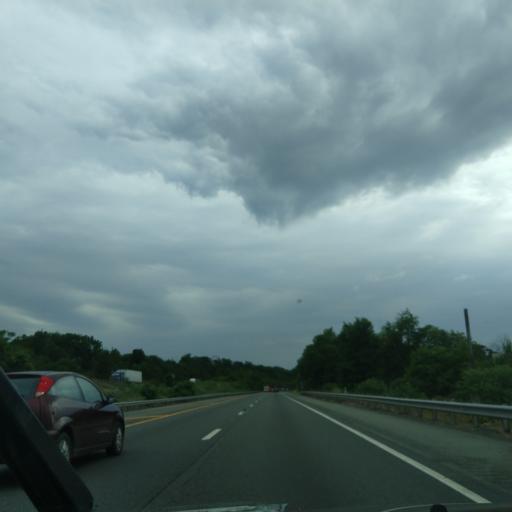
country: US
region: Pennsylvania
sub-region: Luzerne County
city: Laflin
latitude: 41.2791
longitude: -75.7936
